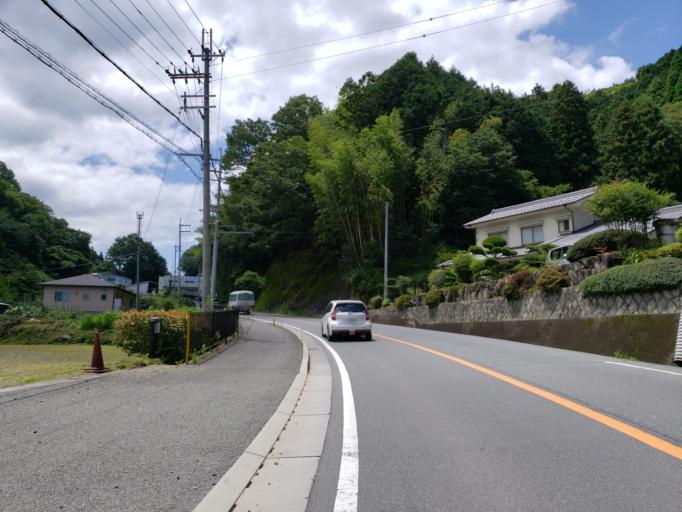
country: JP
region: Hyogo
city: Yamazakicho-nakabirose
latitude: 34.9761
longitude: 134.6493
